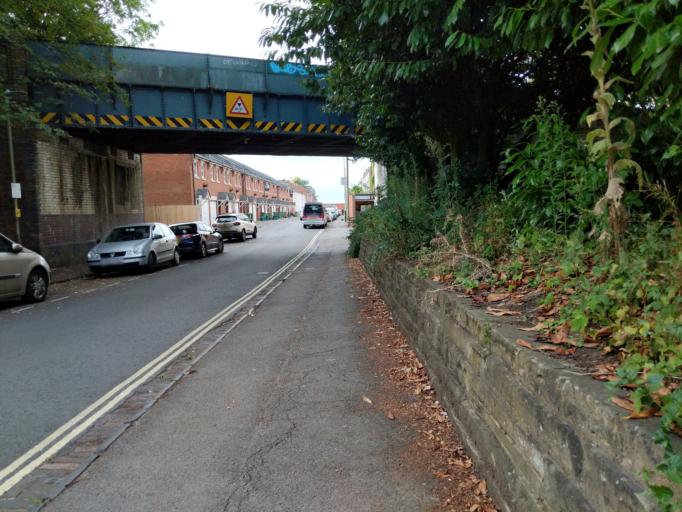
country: GB
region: England
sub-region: Gloucestershire
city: Cheltenham
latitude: 51.9037
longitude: -2.0852
